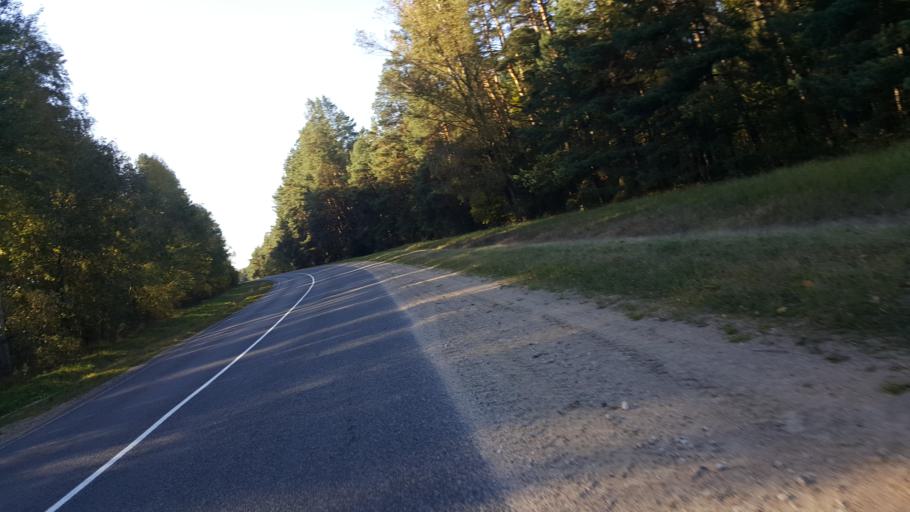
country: BY
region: Brest
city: Kamyanyets
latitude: 52.3846
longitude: 23.8576
